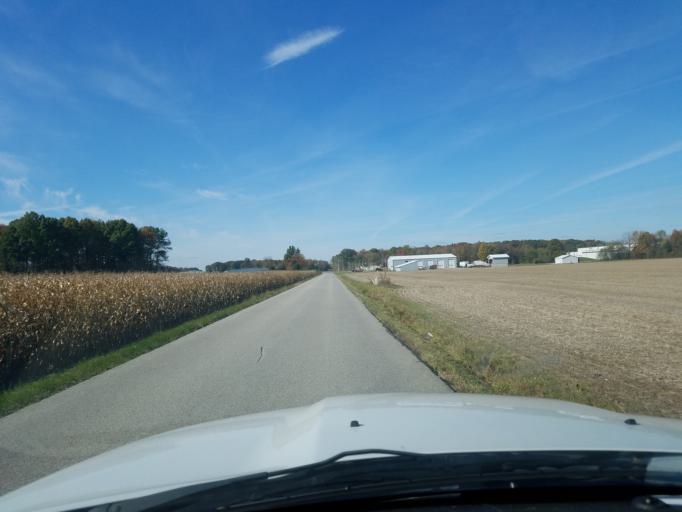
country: US
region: Indiana
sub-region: Jennings County
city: North Vernon
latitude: 39.0365
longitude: -85.6181
